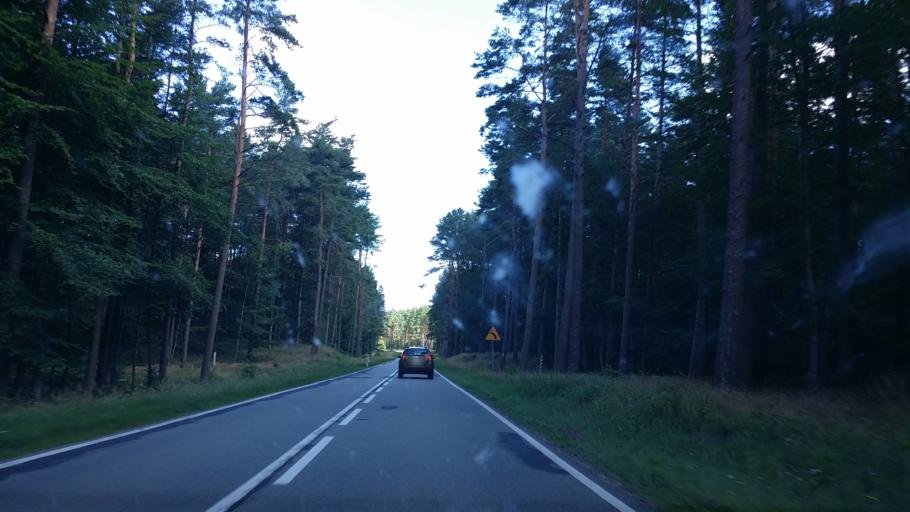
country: PL
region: West Pomeranian Voivodeship
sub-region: Powiat drawski
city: Drawsko Pomorskie
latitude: 53.4276
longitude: 15.8269
